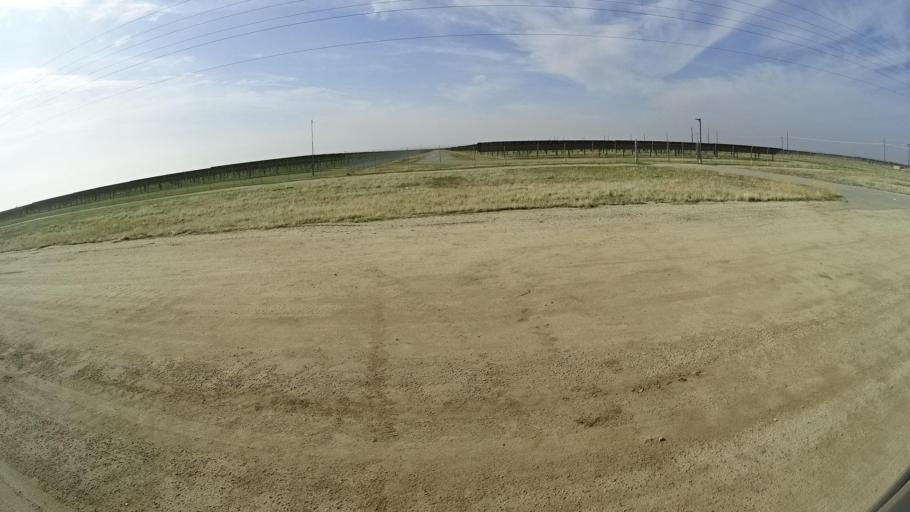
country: US
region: California
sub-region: Kern County
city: Arvin
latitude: 35.3239
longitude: -118.8075
